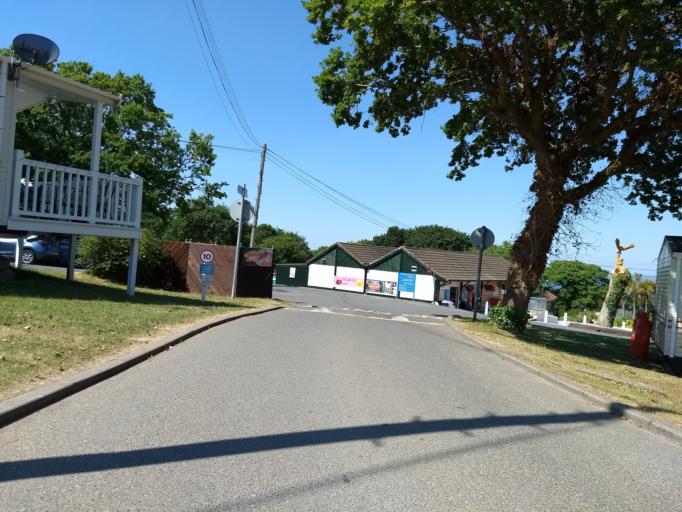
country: GB
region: England
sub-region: Isle of Wight
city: Gurnard
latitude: 50.7346
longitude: -1.3606
